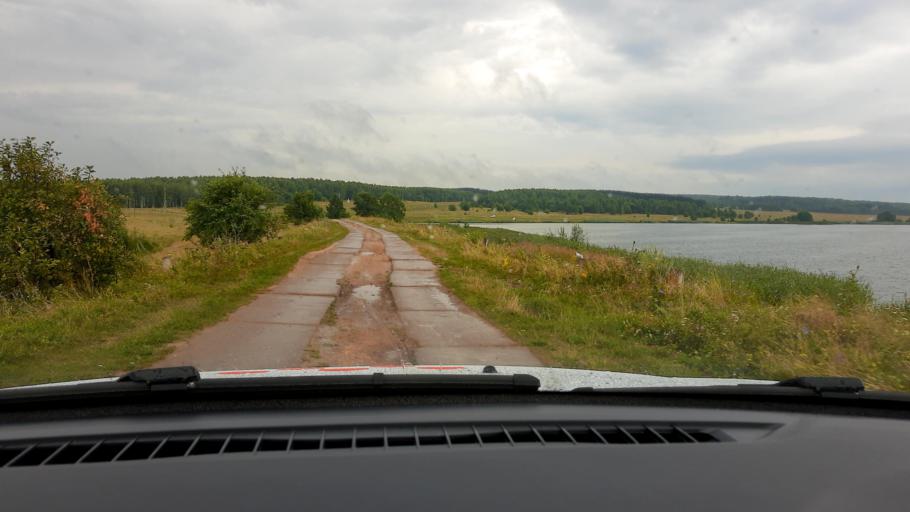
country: RU
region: Nizjnij Novgorod
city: Surovatikha
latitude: 55.9358
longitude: 43.9171
